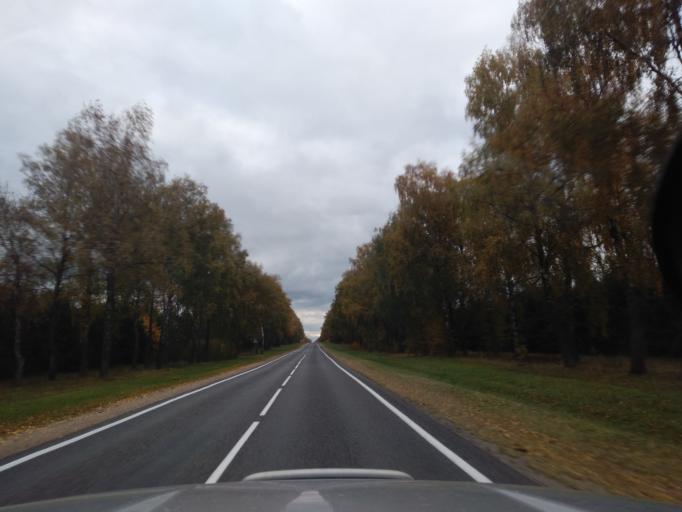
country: BY
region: Minsk
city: Slutsk
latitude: 53.2217
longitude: 27.4991
